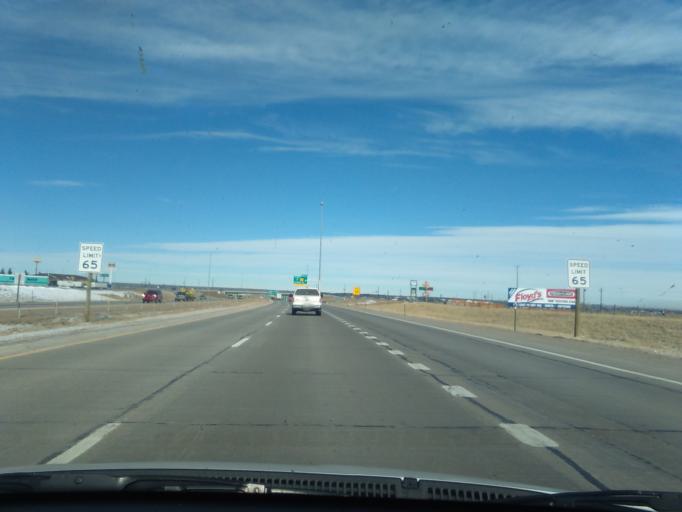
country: US
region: Wyoming
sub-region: Laramie County
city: South Greeley
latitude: 41.0941
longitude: -104.8502
